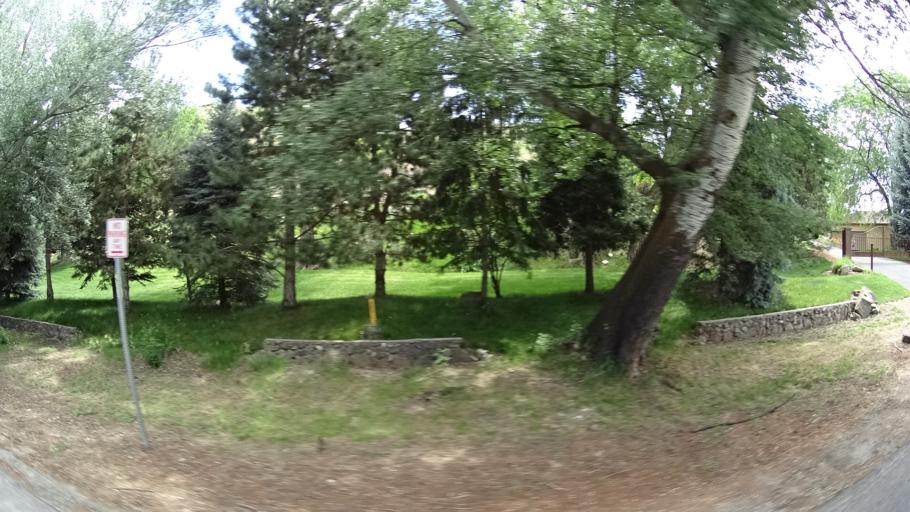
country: US
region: Idaho
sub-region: Ada County
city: Boise
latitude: 43.5926
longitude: -116.1636
